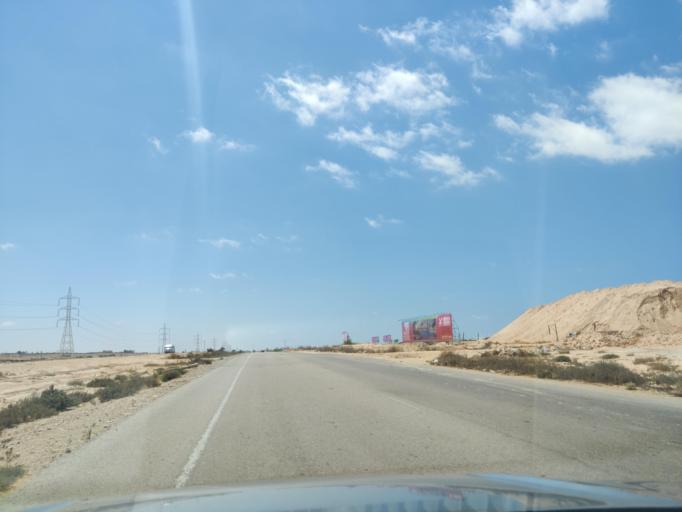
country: EG
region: Muhafazat Matruh
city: Al `Alamayn
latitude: 31.0651
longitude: 28.1884
